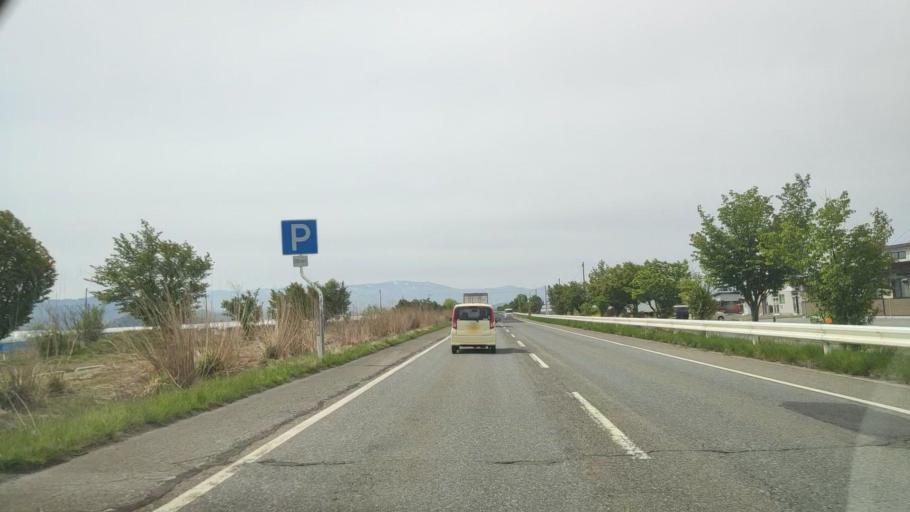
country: JP
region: Yamagata
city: Takahata
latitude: 38.0429
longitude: 140.1749
